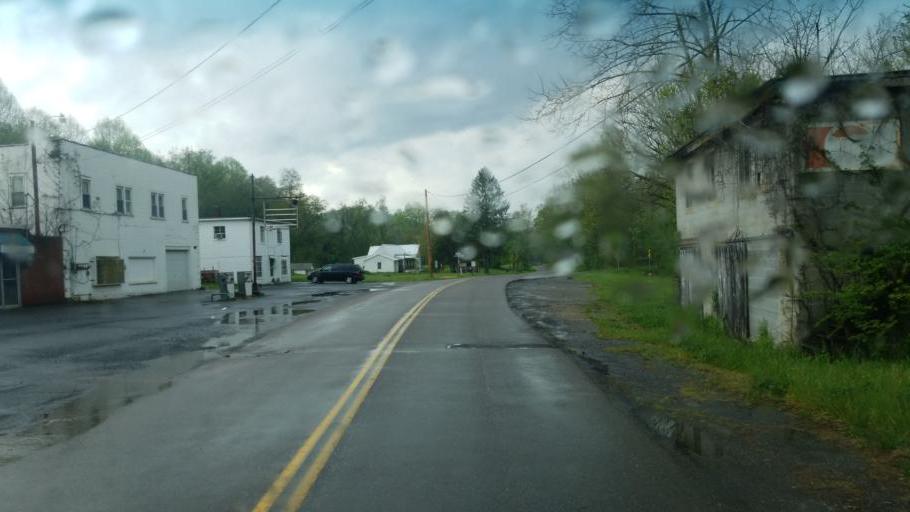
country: US
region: Virginia
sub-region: Smyth County
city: Adwolf
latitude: 36.7682
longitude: -81.5658
